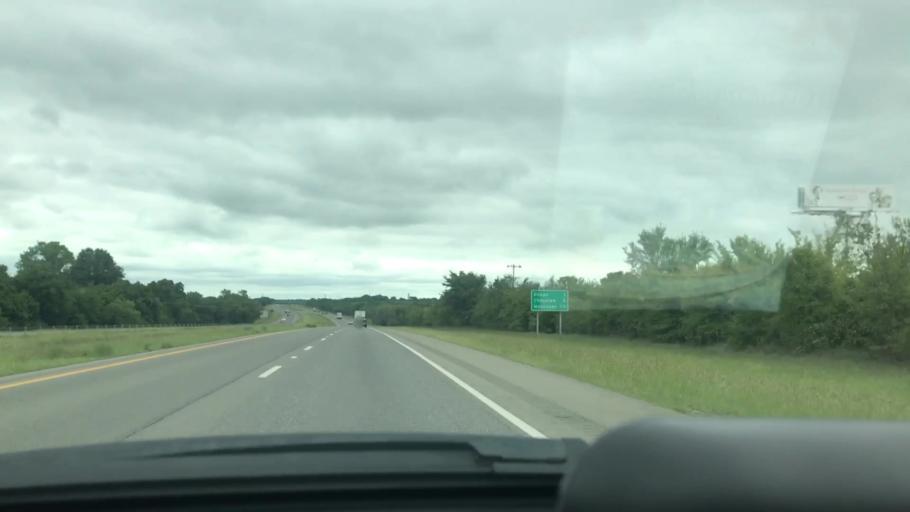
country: US
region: Oklahoma
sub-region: McIntosh County
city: Eufaula
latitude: 35.3738
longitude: -95.5704
